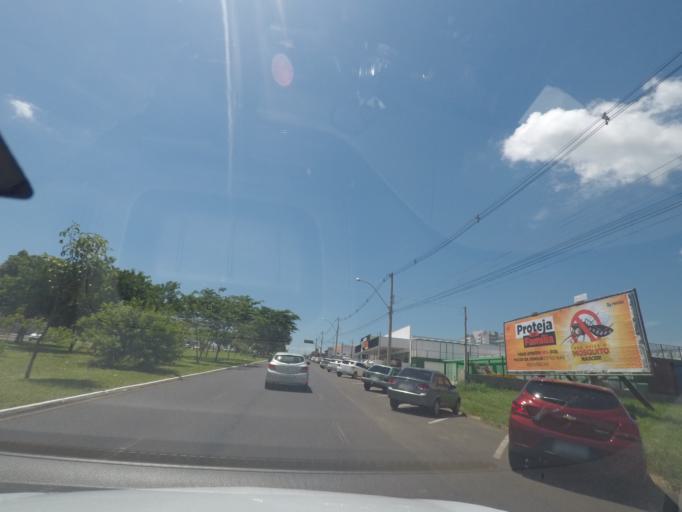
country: BR
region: Sao Paulo
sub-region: Matao
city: Matao
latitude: -21.6194
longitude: -48.3584
